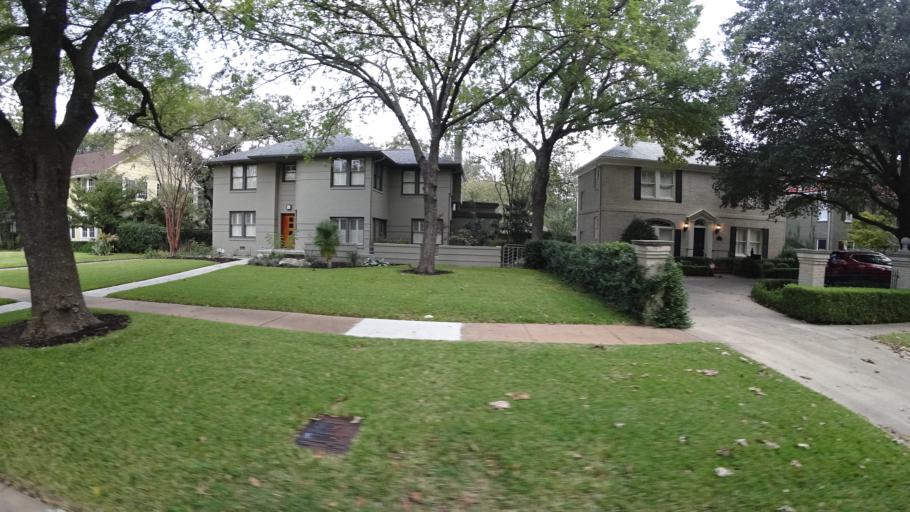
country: US
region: Texas
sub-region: Travis County
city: Austin
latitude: 30.2929
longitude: -97.7541
